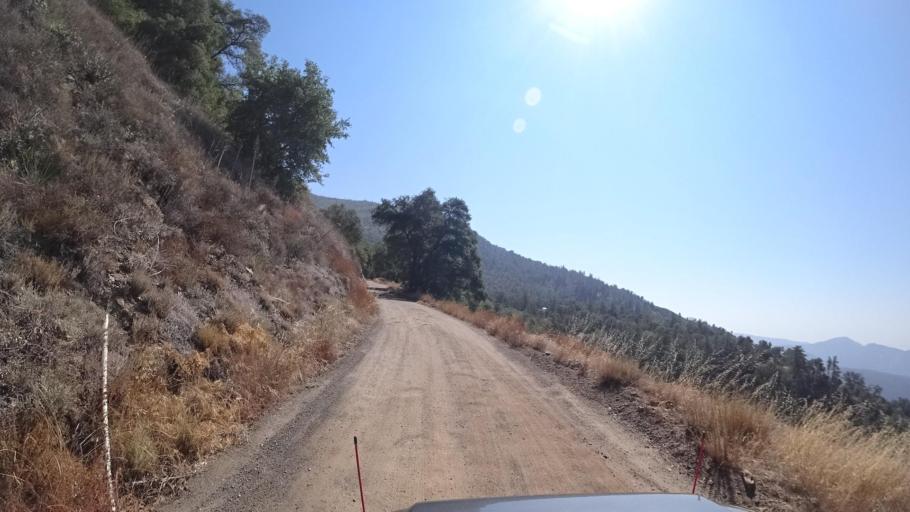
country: US
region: California
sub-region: Riverside County
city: Aguanga
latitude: 33.3333
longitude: -116.9423
